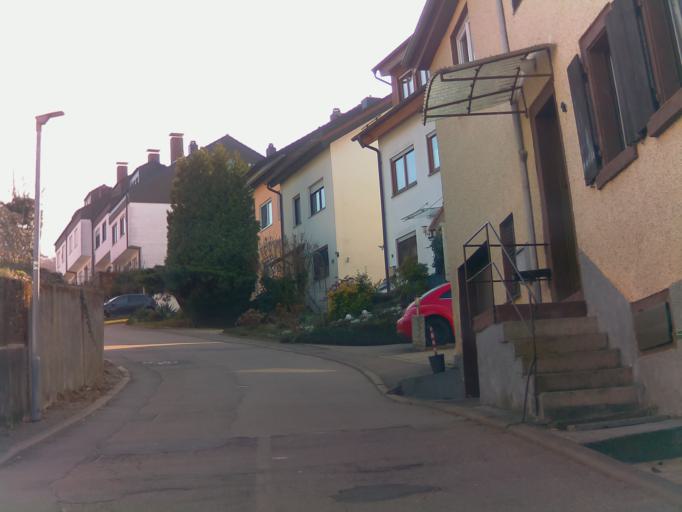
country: DE
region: Baden-Wuerttemberg
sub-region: Karlsruhe Region
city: Wilhelmsfeld
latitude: 49.5104
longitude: 8.7462
